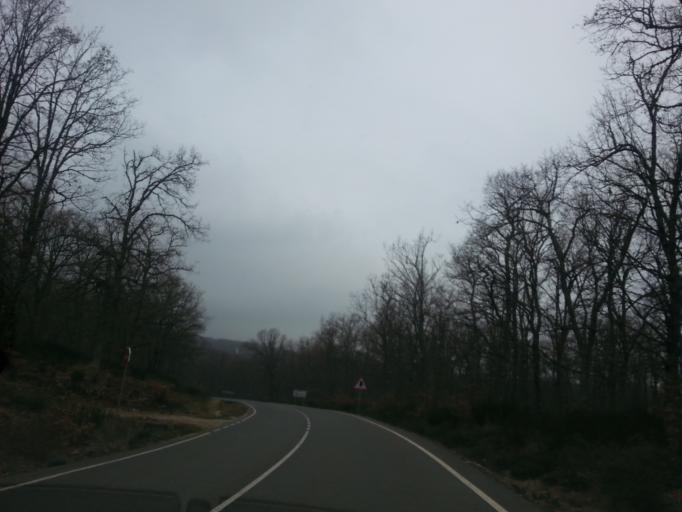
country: ES
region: Castille and Leon
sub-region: Provincia de Salamanca
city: Monforte de la Sierra
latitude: 40.4792
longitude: -6.0764
